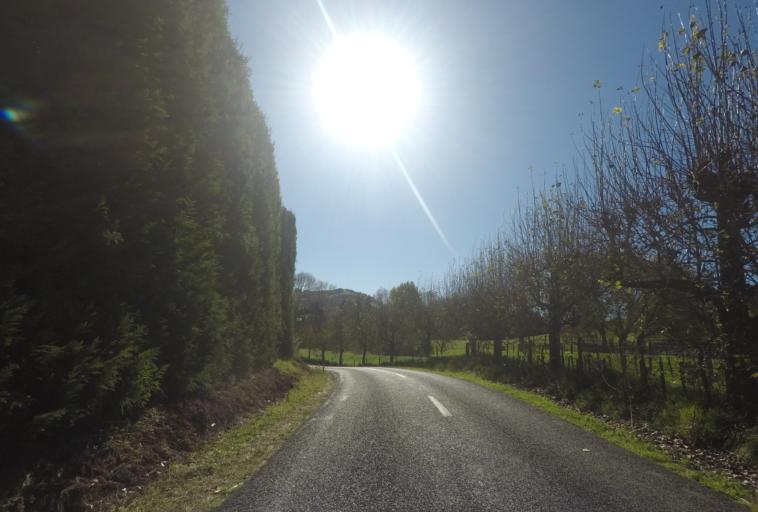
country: NZ
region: Bay of Plenty
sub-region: Western Bay of Plenty District
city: Waihi Beach
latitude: -37.4017
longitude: 175.9060
